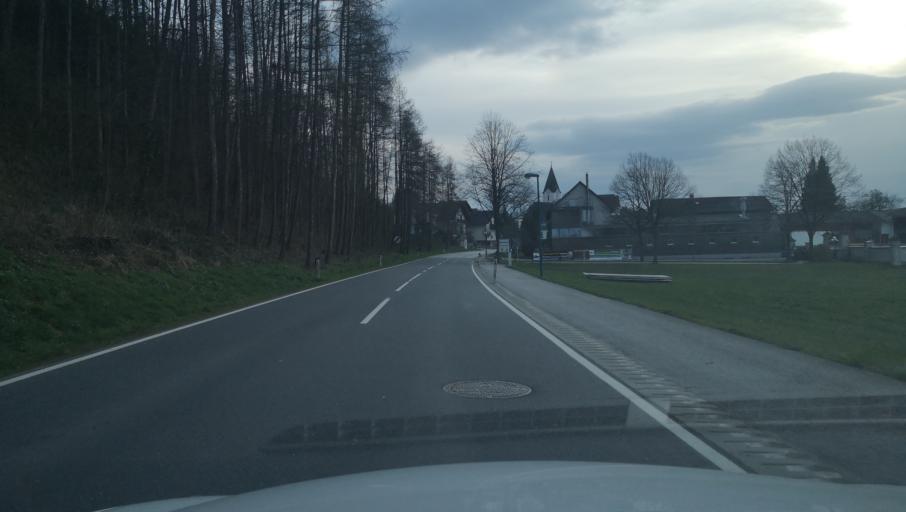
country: AT
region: Lower Austria
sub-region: Politischer Bezirk Amstetten
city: Winklarn
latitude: 48.0934
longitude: 14.8510
